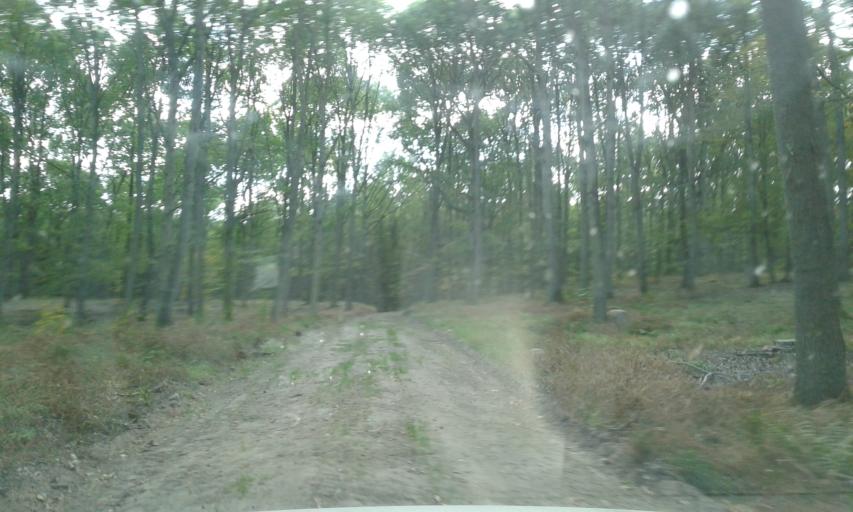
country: PL
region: West Pomeranian Voivodeship
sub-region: Powiat stargardzki
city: Dolice
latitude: 53.2317
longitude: 15.2453
